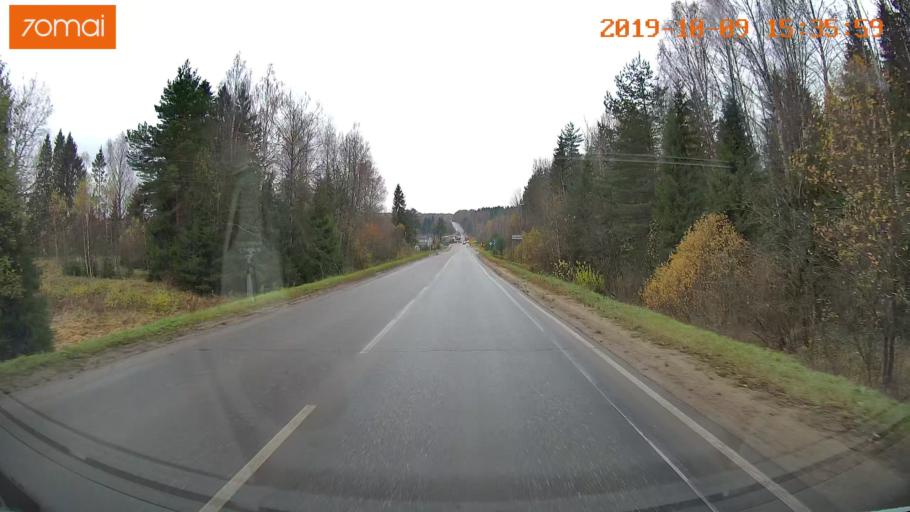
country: RU
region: Kostroma
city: Oktyabr'skiy
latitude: 57.9268
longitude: 41.2166
